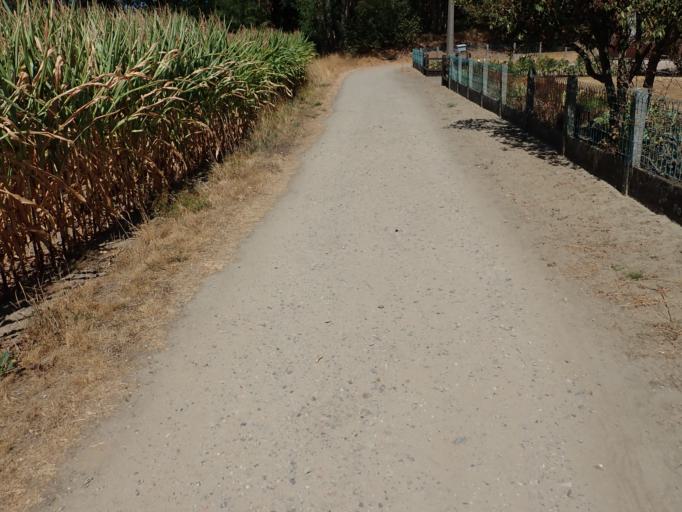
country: BE
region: Flanders
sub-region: Provincie Vlaams-Brabant
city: Haacht
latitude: 50.9796
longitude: 4.6436
